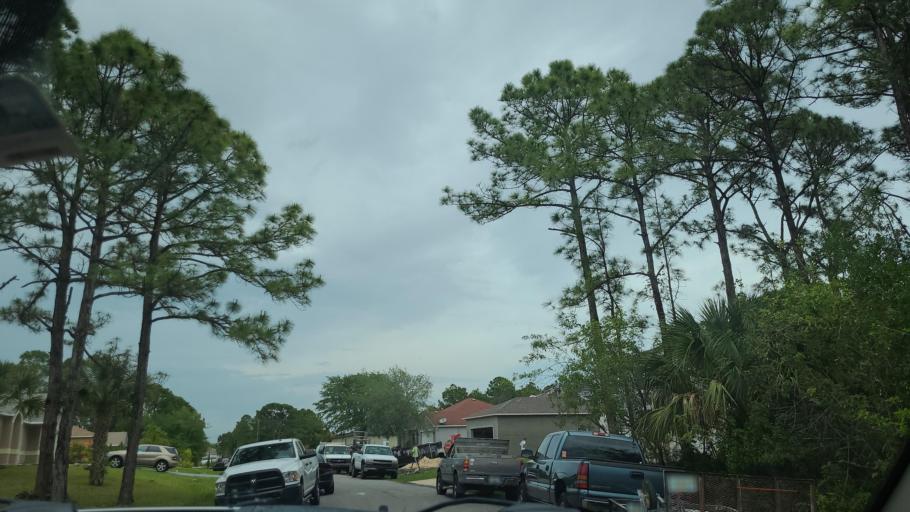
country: US
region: Florida
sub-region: Brevard County
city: Grant-Valkaria
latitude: 27.9403
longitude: -80.6267
